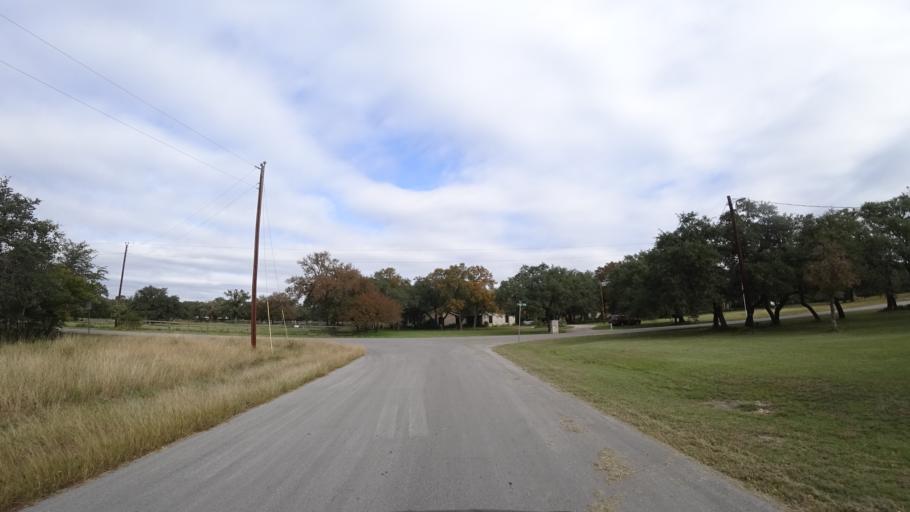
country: US
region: Texas
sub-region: Travis County
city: Shady Hollow
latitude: 30.1457
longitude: -97.8858
